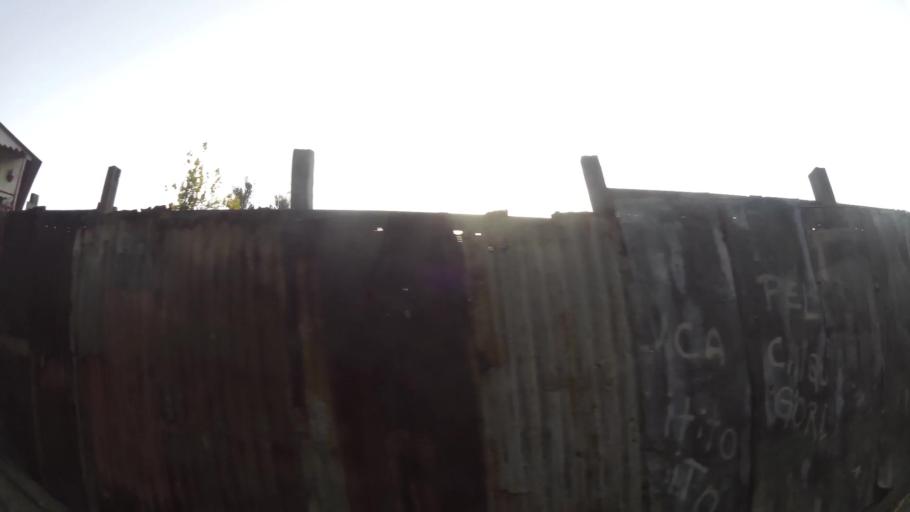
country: CL
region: Valparaiso
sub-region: Provincia de Valparaiso
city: Valparaiso
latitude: -33.0608
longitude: -71.6048
